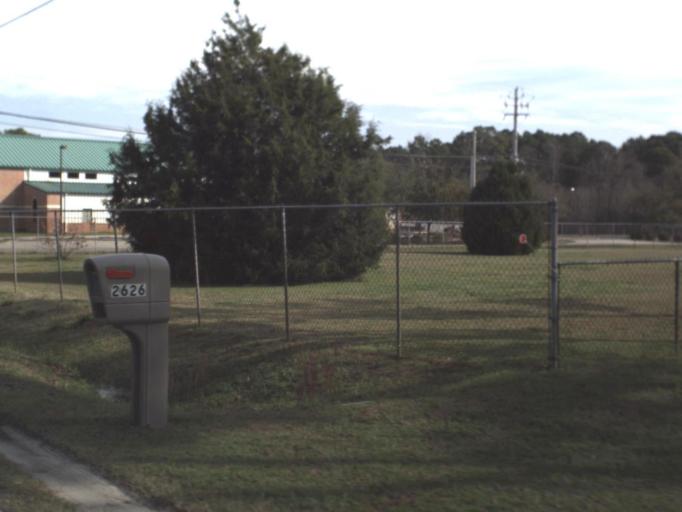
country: US
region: Florida
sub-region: Bay County
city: Pretty Bayou
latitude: 30.1966
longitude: -85.6833
